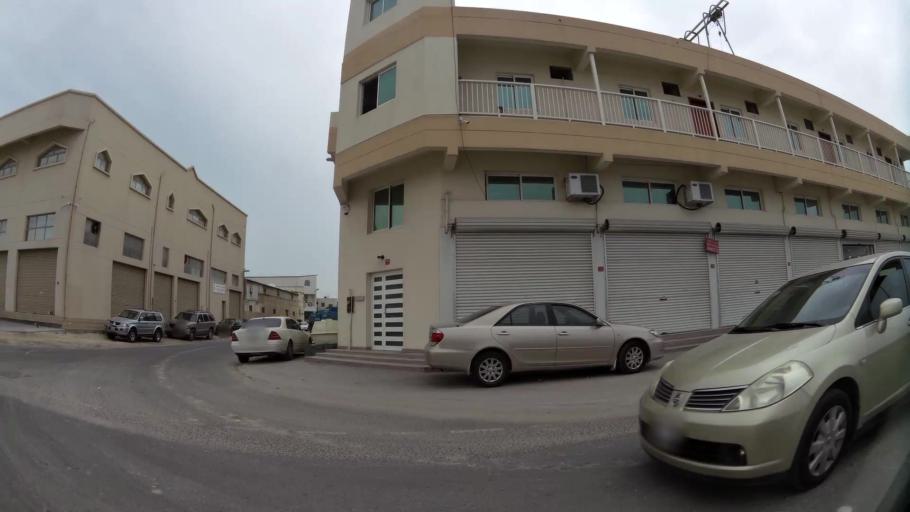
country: BH
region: Northern
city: Madinat `Isa
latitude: 26.1783
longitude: 50.5347
